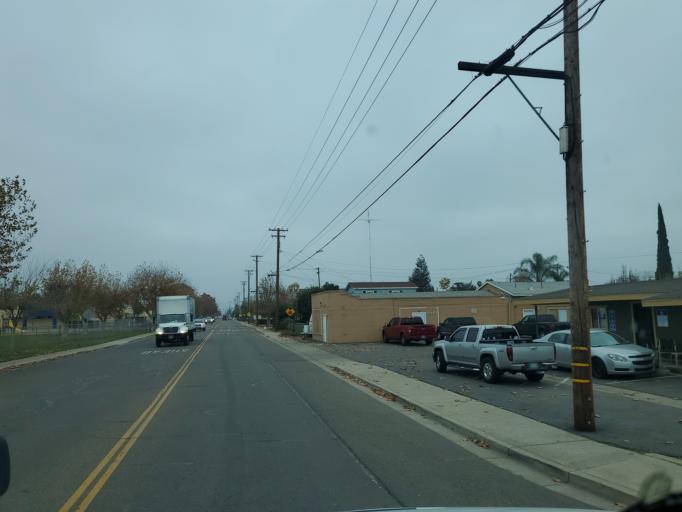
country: US
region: California
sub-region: Stanislaus County
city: Hughson
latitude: 37.5948
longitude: -120.8654
